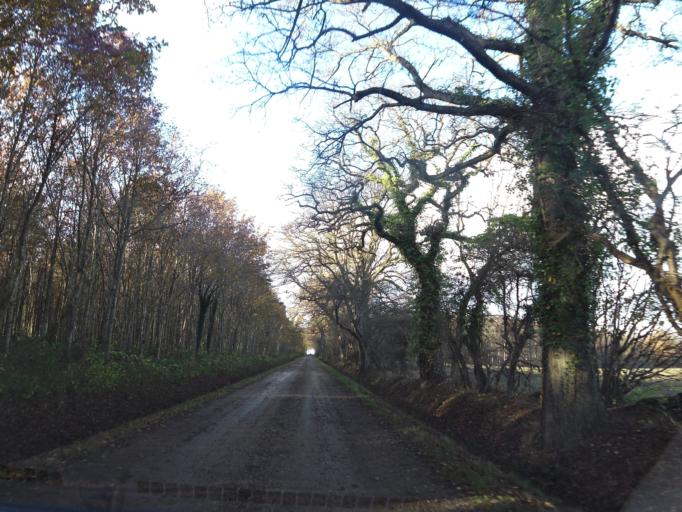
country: DK
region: Central Jutland
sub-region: Odder Kommune
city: Odder
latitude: 55.8541
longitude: 10.1671
